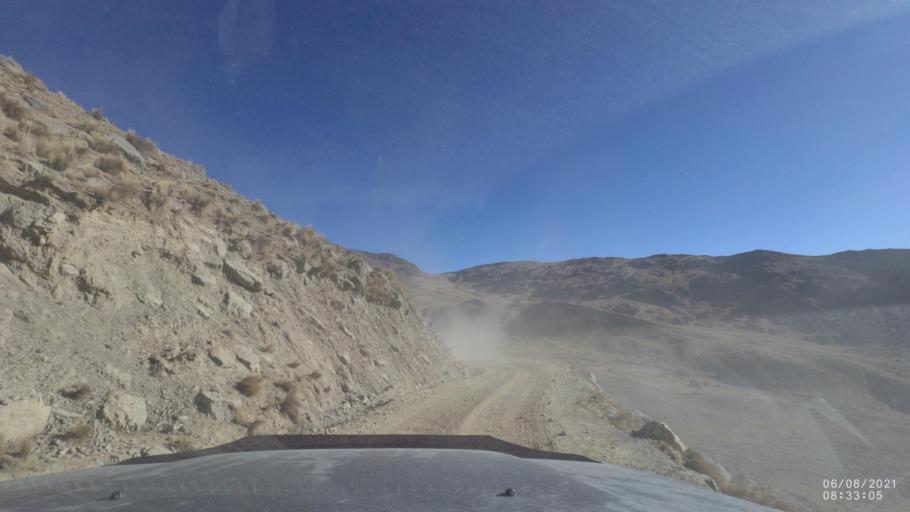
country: BO
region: Cochabamba
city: Sipe Sipe
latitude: -17.1813
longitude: -66.3761
